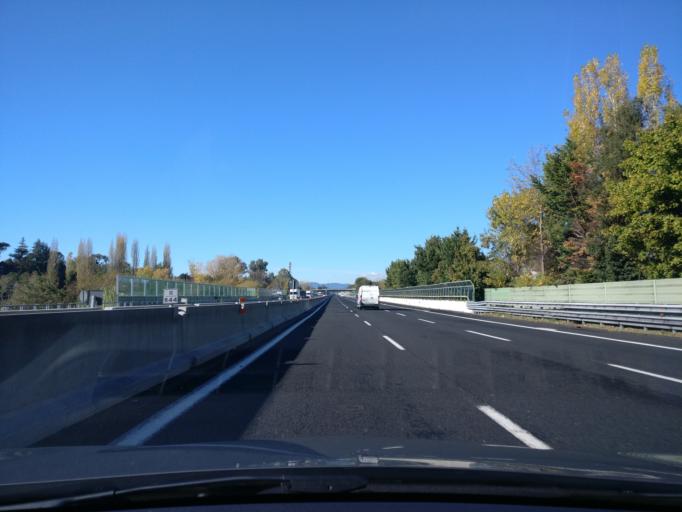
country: IT
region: Latium
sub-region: Provincia di Frosinone
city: Ceprano
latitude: 41.5430
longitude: 13.5157
